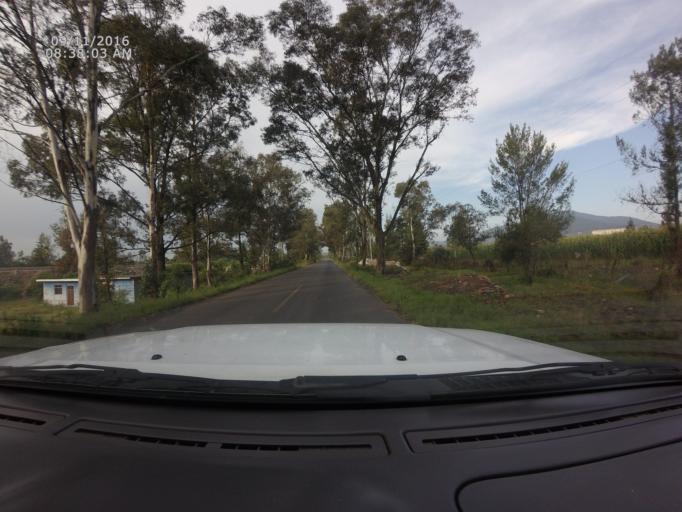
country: MX
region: Michoacan
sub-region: Morelia
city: La Mintzita (Piedra Dura)
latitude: 19.6219
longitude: -101.2776
